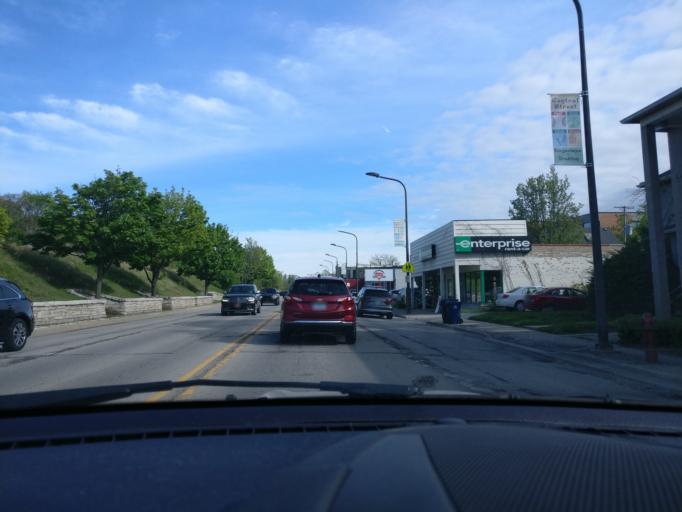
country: US
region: Illinois
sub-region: Cook County
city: Wilmette
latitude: 42.0658
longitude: -87.7001
